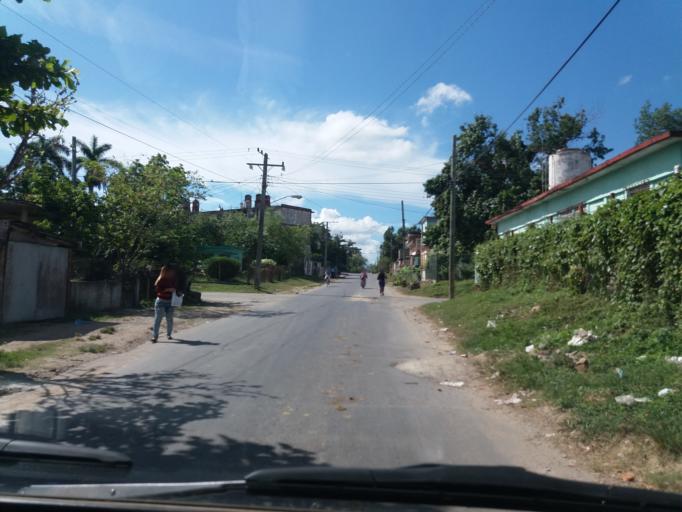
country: CU
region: Cienfuegos
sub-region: Municipio de Cienfuegos
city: Cienfuegos
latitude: 22.1511
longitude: -80.4280
